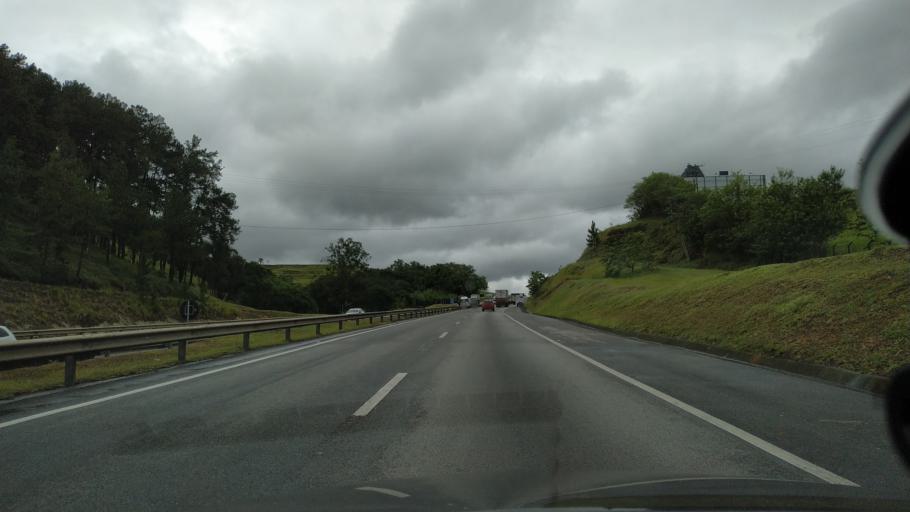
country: BR
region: Sao Paulo
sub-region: Santa Isabel
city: Santa Isabel
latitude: -23.3477
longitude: -46.1681
